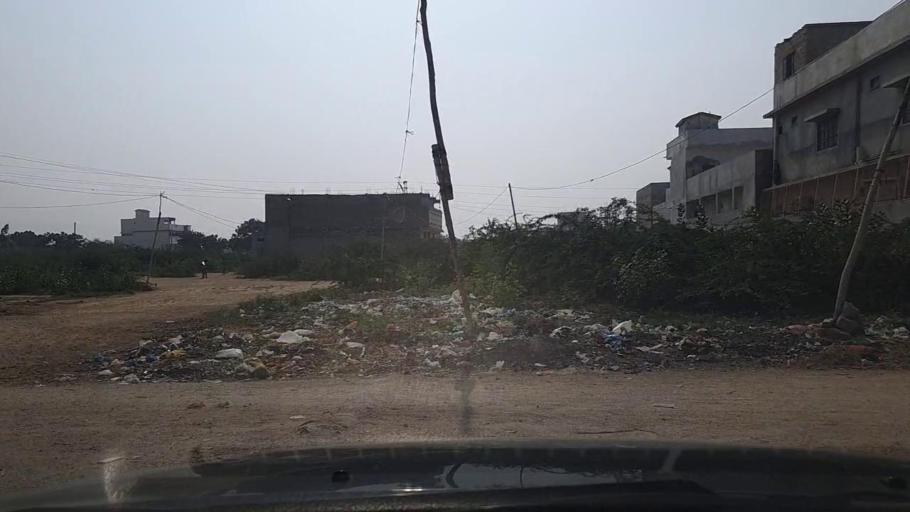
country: PK
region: Sindh
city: Thatta
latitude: 24.7391
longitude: 67.8982
